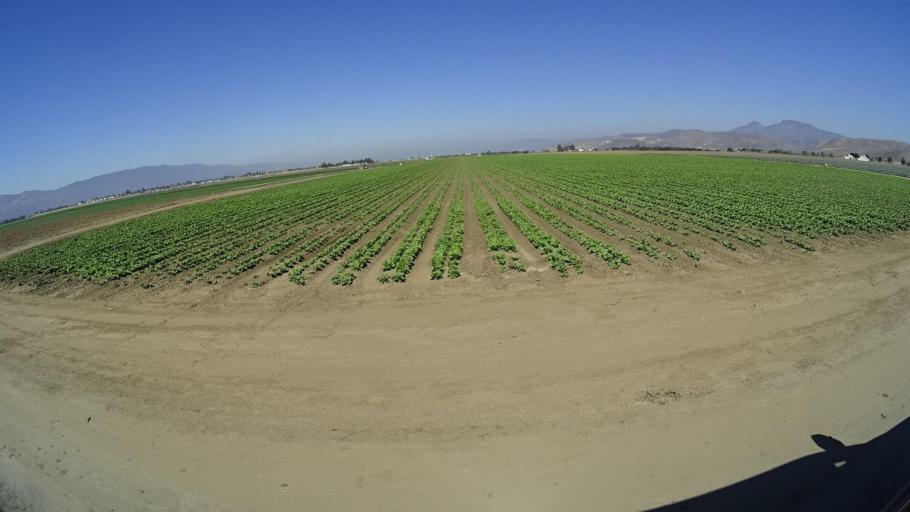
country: US
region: California
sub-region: Monterey County
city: Greenfield
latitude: 36.3197
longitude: -121.2085
